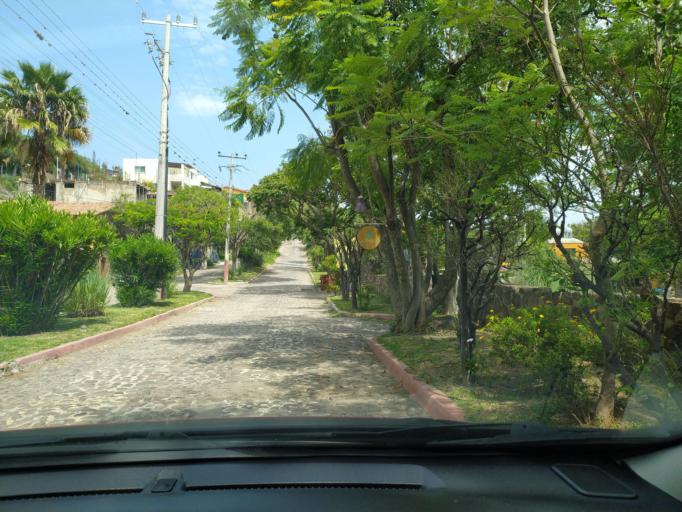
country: MX
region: Jalisco
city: San Juan Cosala
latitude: 20.2906
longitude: -103.3295
